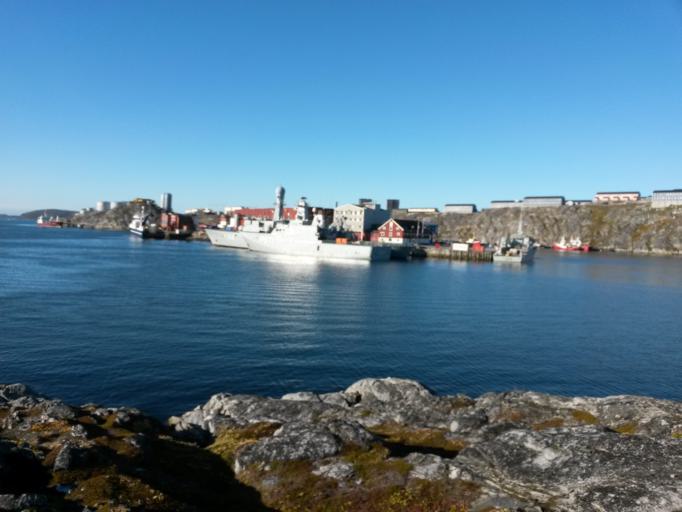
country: GL
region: Sermersooq
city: Nuuk
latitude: 64.1724
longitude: -51.7158
